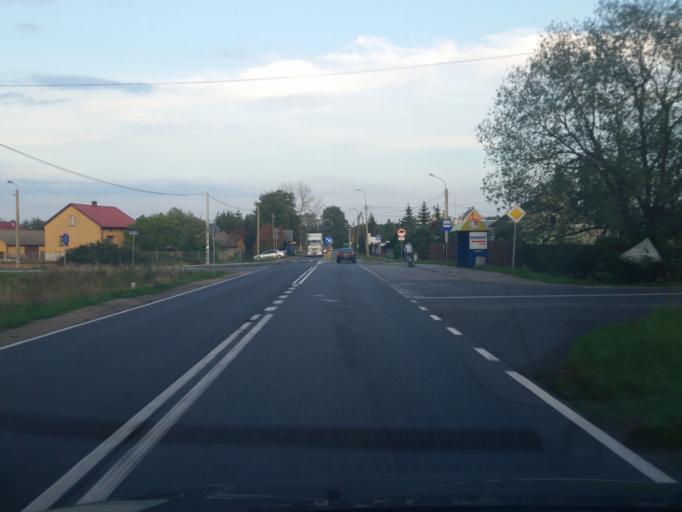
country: PL
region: Masovian Voivodeship
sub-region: Powiat nowodworski
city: Zakroczym
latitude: 52.3945
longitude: 20.6585
